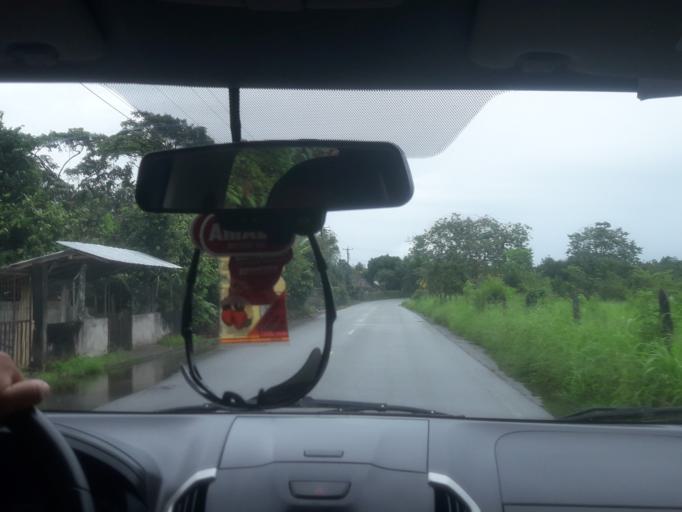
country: EC
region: Napo
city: Tena
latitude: -1.0336
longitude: -77.7466
